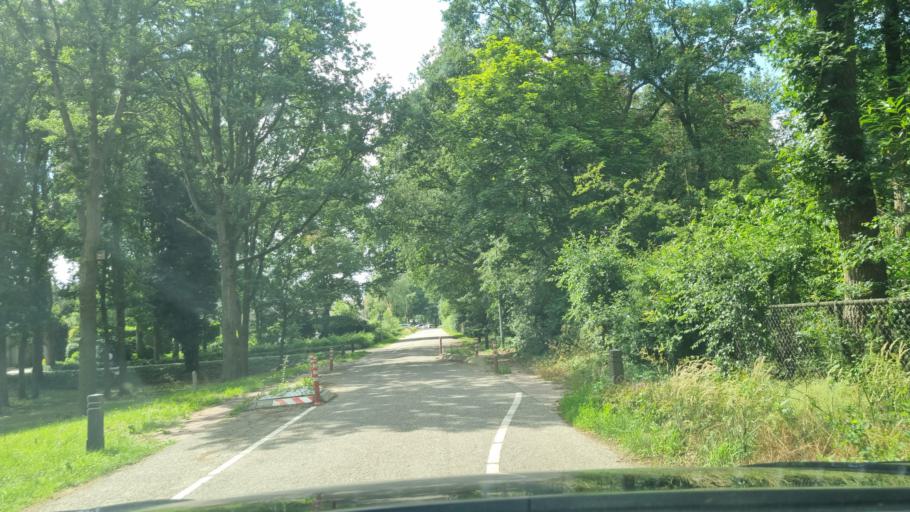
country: NL
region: Gelderland
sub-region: Gemeente Groesbeek
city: Bredeweg
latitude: 51.7264
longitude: 5.9216
